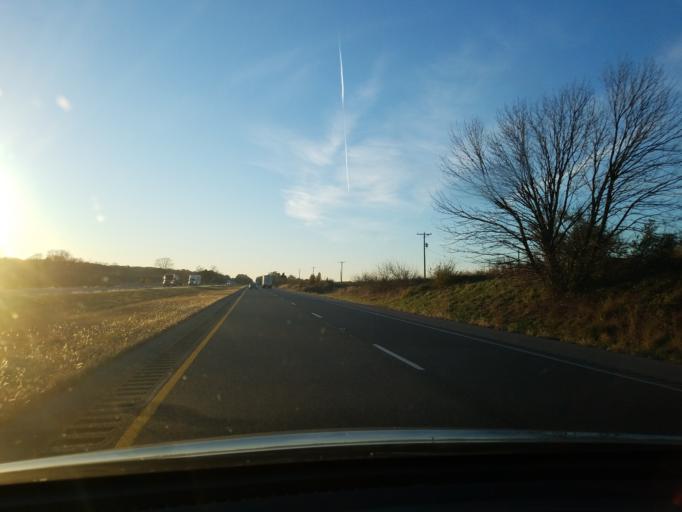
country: US
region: Indiana
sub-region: Gibson County
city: Haubstadt
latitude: 38.1671
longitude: -87.5928
